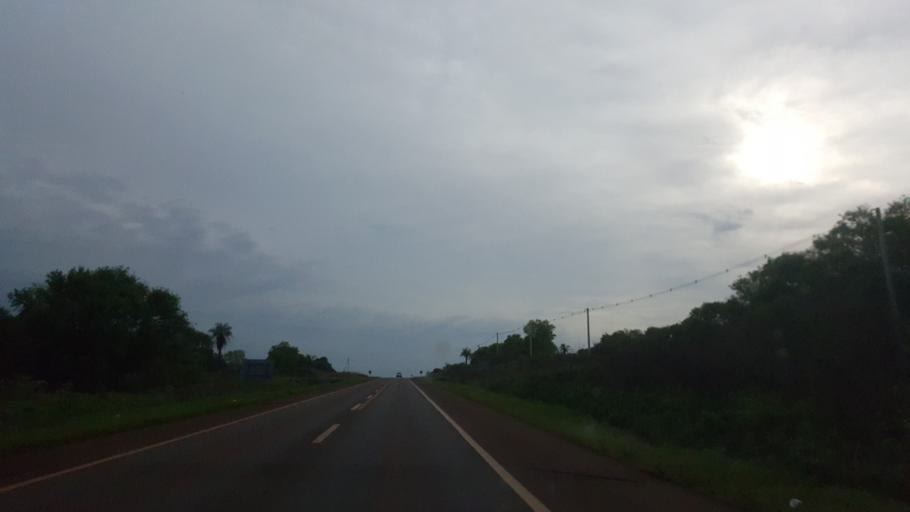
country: AR
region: Misiones
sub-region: Departamento de Apostoles
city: San Jose
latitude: -27.7628
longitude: -55.7951
